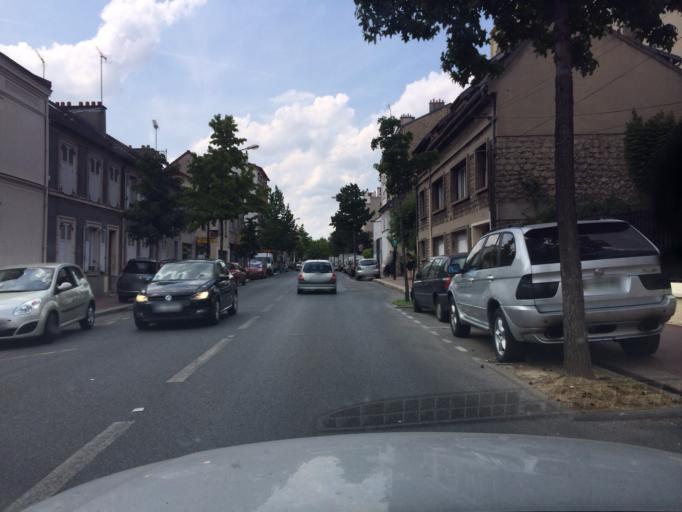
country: FR
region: Ile-de-France
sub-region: Departement du Val-de-Marne
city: Saint-Maur-des-Fosses
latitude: 48.7982
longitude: 2.4795
